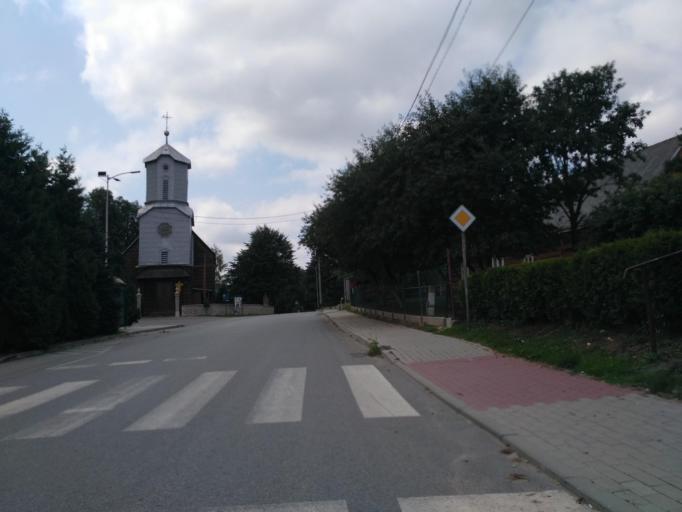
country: PL
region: Subcarpathian Voivodeship
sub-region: Powiat krosnienski
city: Iwonicz-Zdroj
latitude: 49.5811
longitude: 21.8240
